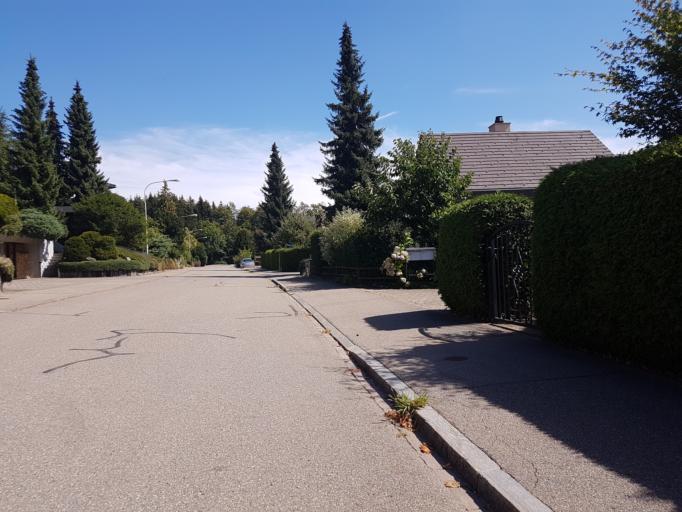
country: CH
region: Zurich
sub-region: Bezirk Pfaeffikon
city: Effretikon / Watt
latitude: 47.4255
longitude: 8.7001
